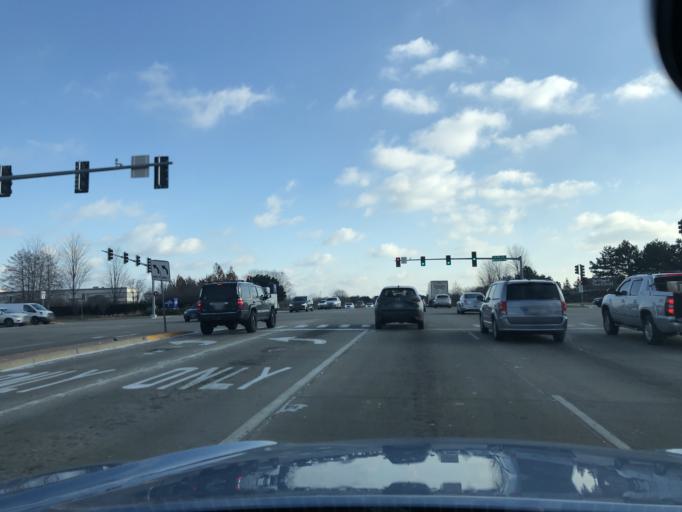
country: US
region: Illinois
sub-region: Cook County
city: Northfield
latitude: 42.1053
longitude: -87.7996
